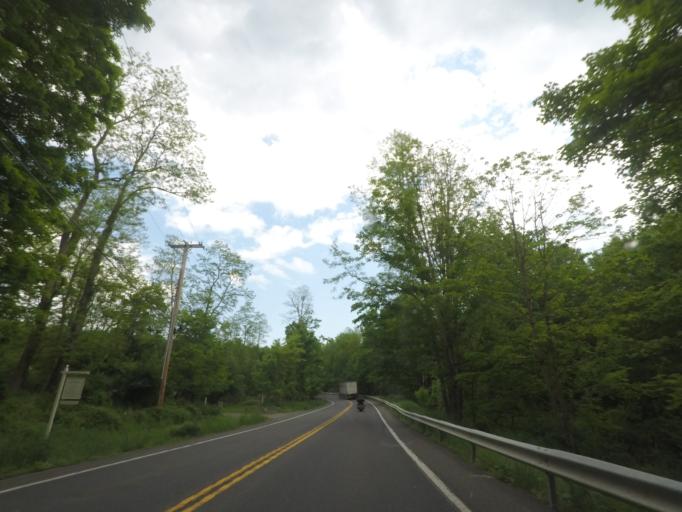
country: US
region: New York
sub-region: Dutchess County
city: Pine Plains
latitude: 42.0556
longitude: -73.6531
